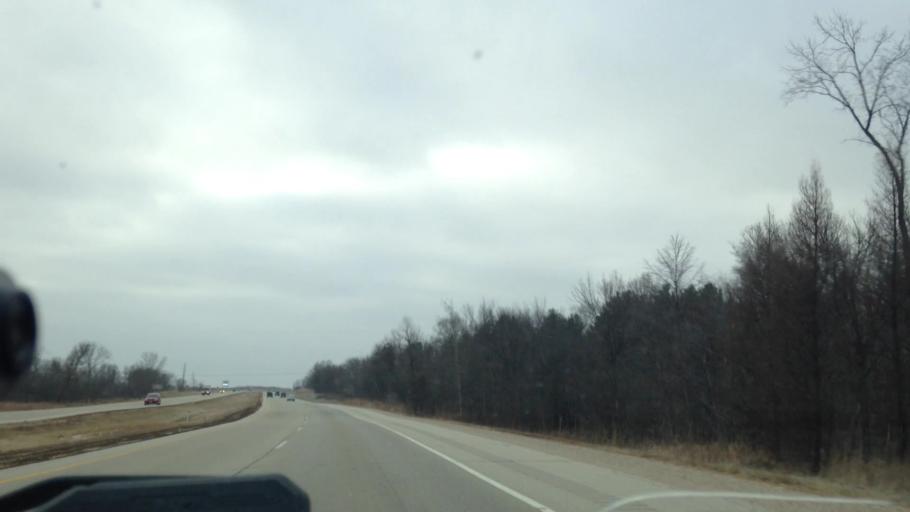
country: US
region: Wisconsin
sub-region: Washington County
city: Jackson
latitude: 43.3690
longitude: -88.1941
